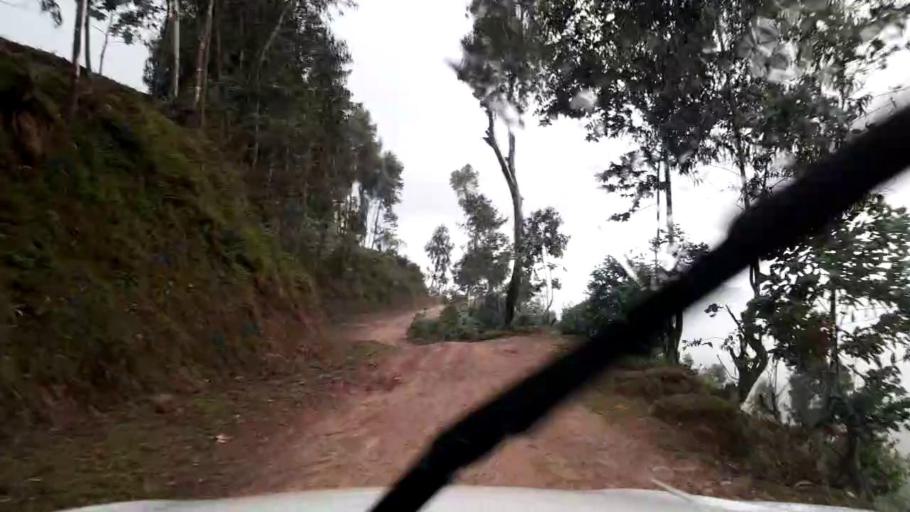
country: RW
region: Western Province
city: Kibuye
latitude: -1.9720
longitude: 29.4871
